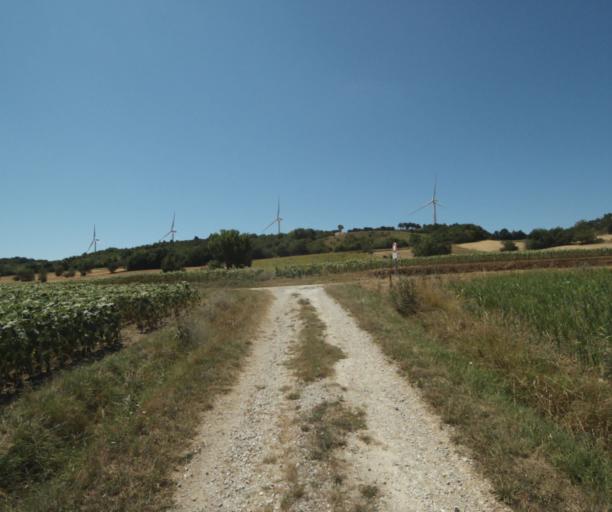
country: FR
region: Midi-Pyrenees
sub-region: Departement de la Haute-Garonne
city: Saint-Felix-Lauragais
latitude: 43.4700
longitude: 1.9237
